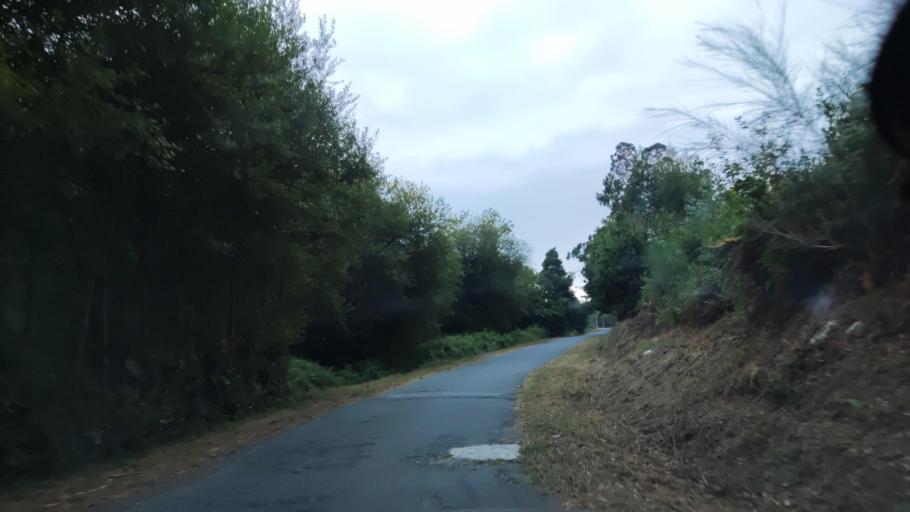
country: ES
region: Galicia
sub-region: Provincia de Pontevedra
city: Catoira
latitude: 42.7069
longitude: -8.7224
